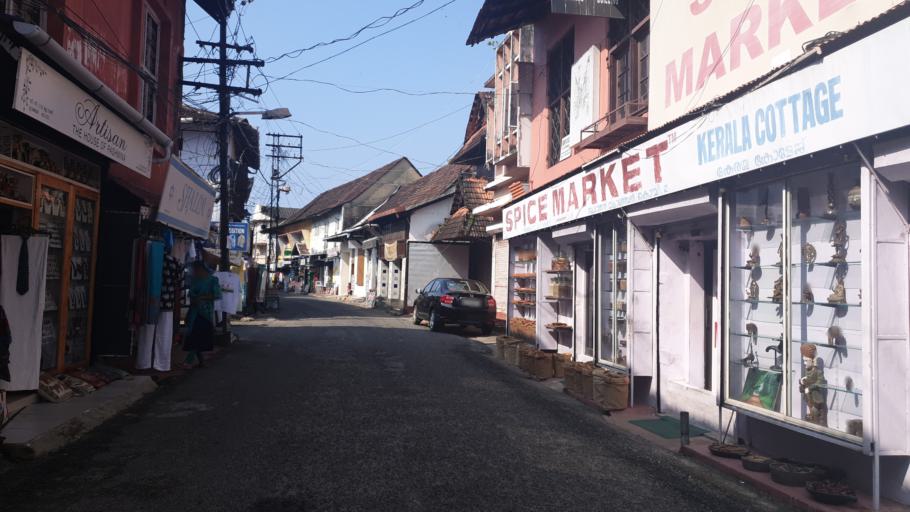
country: IN
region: Kerala
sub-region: Ernakulam
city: Cochin
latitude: 9.9556
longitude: 76.2602
